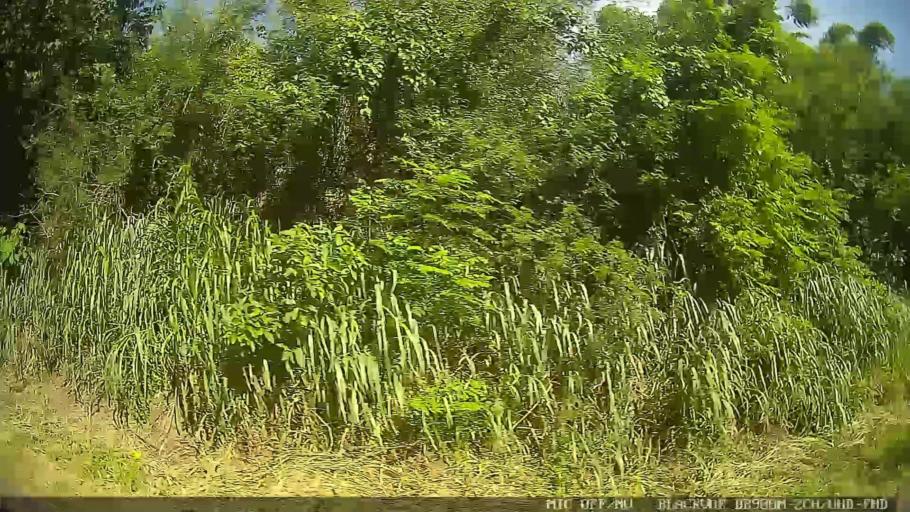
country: BR
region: Sao Paulo
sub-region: Tiete
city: Tiete
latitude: -23.1077
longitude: -47.6947
